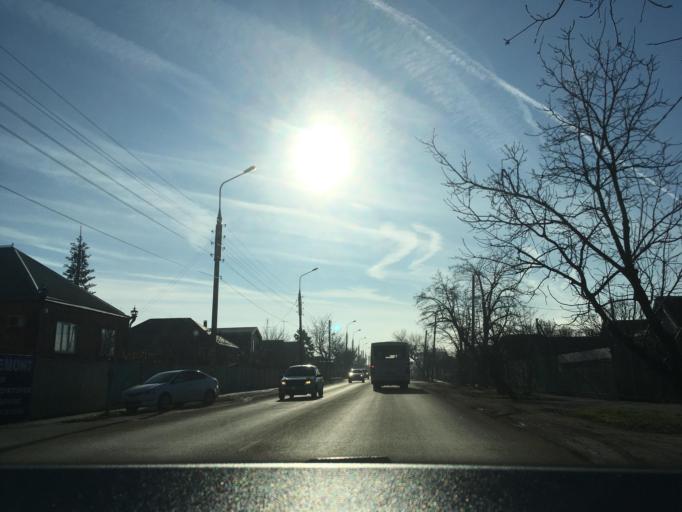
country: RU
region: Krasnodarskiy
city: Krasnodar
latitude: 45.1217
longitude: 39.0113
